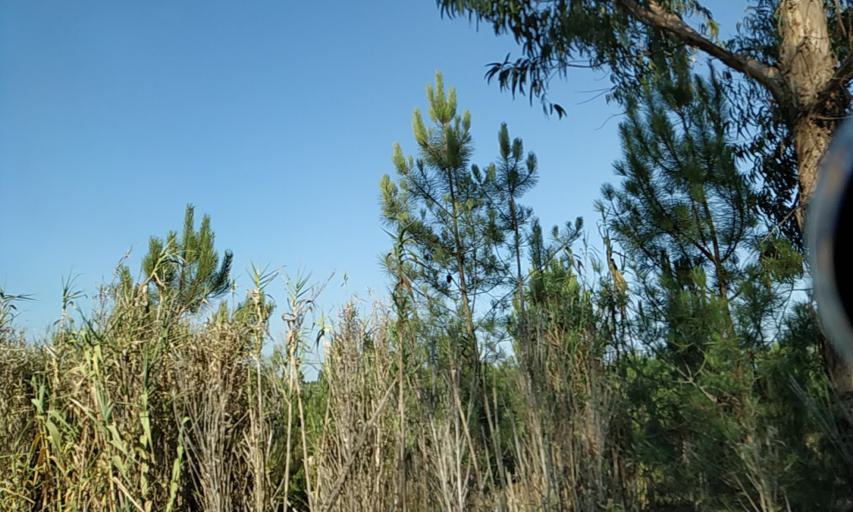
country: PT
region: Santarem
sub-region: Almeirim
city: Fazendas de Almeirim
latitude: 39.0778
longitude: -8.5669
